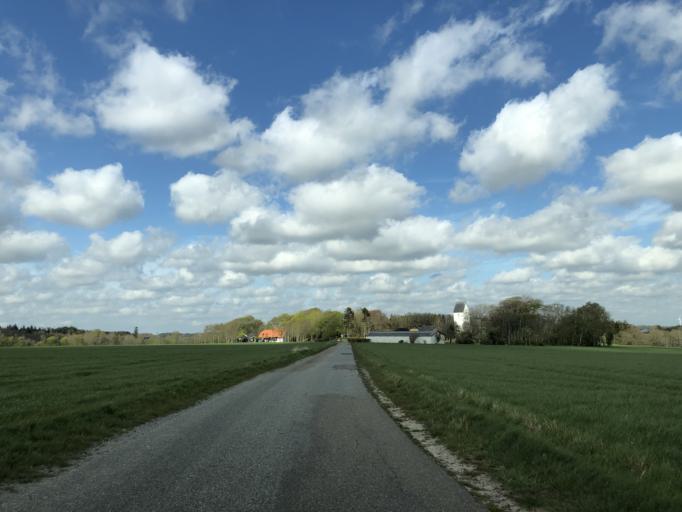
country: DK
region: Central Jutland
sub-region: Holstebro Kommune
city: Holstebro
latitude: 56.2721
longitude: 8.6517
